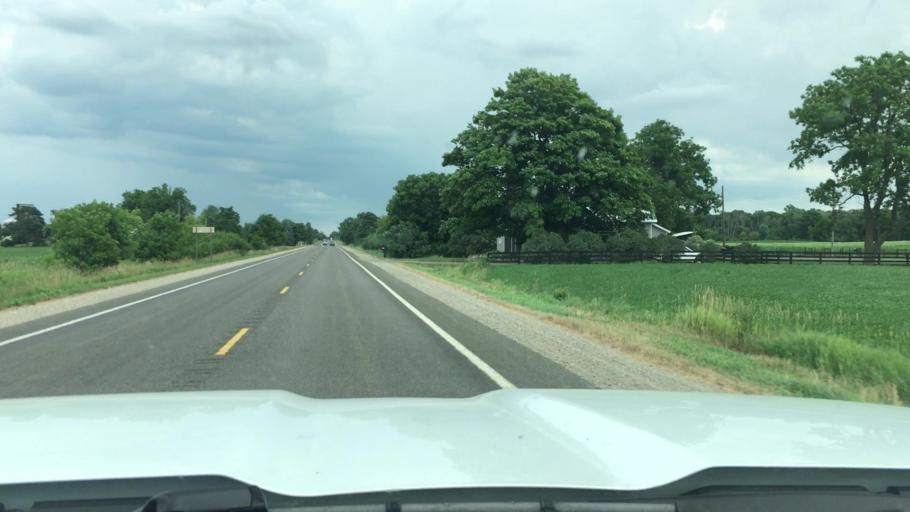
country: US
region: Michigan
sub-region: Montcalm County
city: Carson City
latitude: 43.1776
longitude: -84.9339
